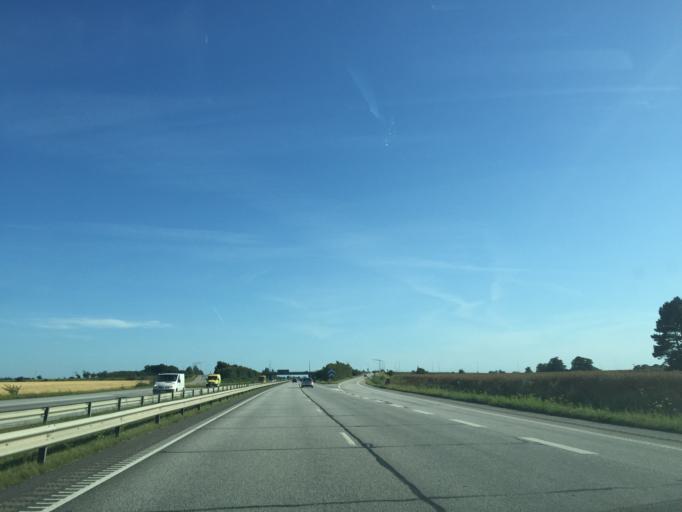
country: SE
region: Skane
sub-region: Malmo
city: Tygelsjo
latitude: 55.5347
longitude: 13.0067
